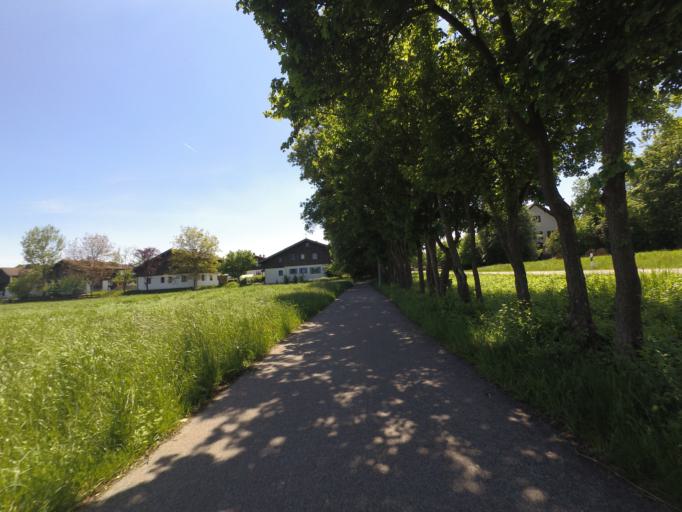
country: DE
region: Bavaria
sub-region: Upper Bavaria
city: Petting
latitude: 47.9175
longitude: 12.8135
